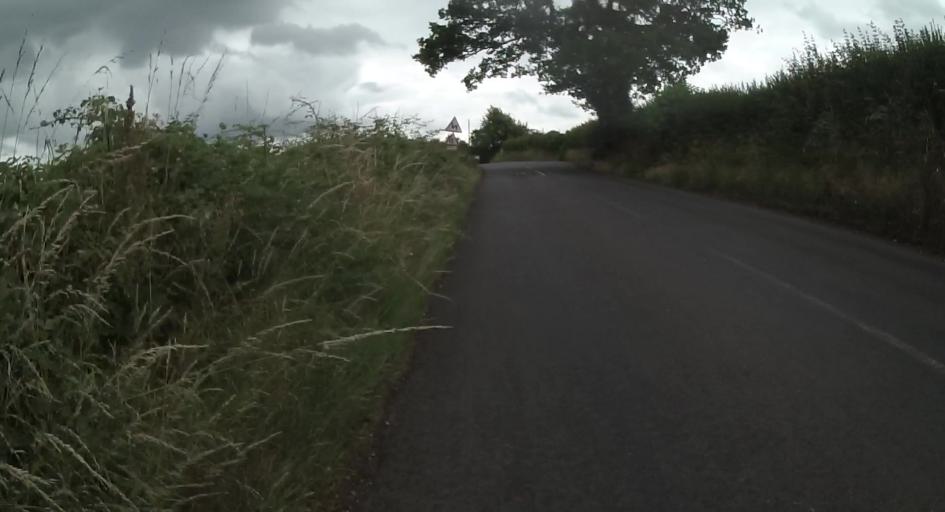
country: GB
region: England
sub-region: Surrey
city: Farnham
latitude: 51.2259
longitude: -0.8542
